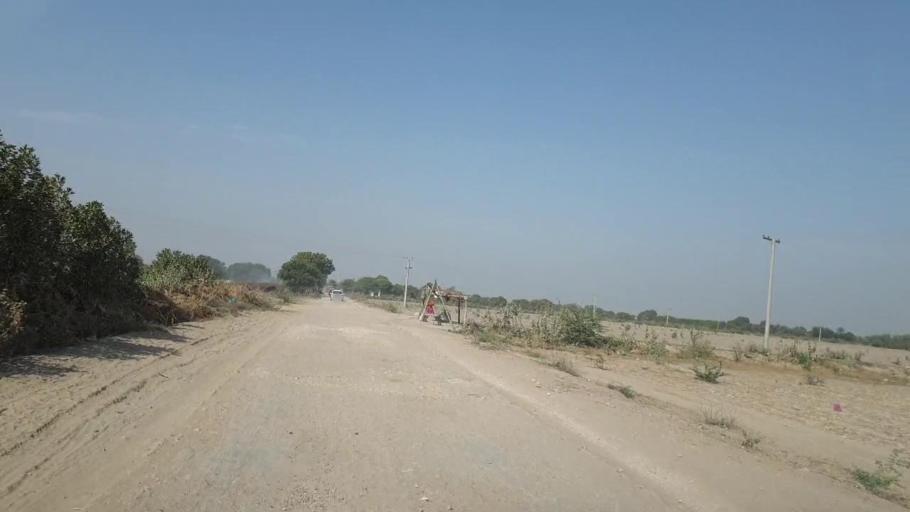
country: PK
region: Sindh
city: Nabisar
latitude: 25.0319
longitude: 69.5245
